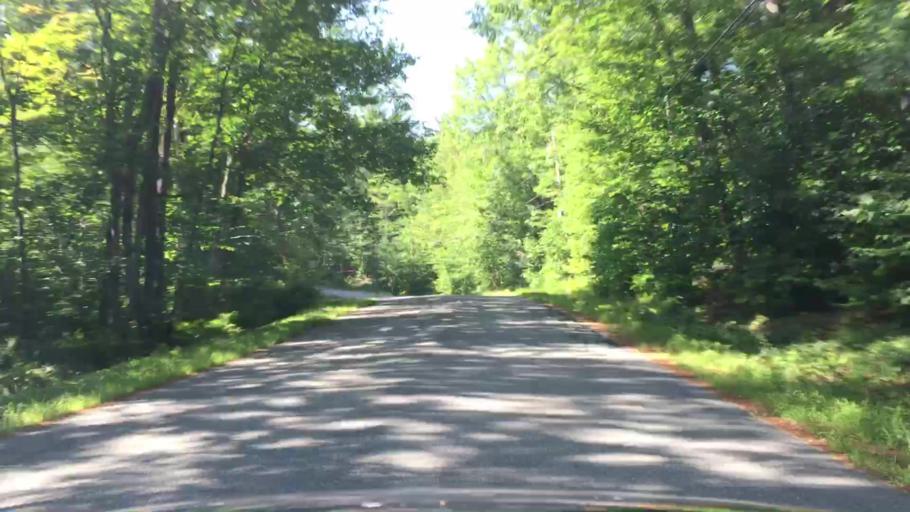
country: US
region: New Hampshire
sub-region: Grafton County
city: Ashland
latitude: 43.7182
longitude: -71.6268
